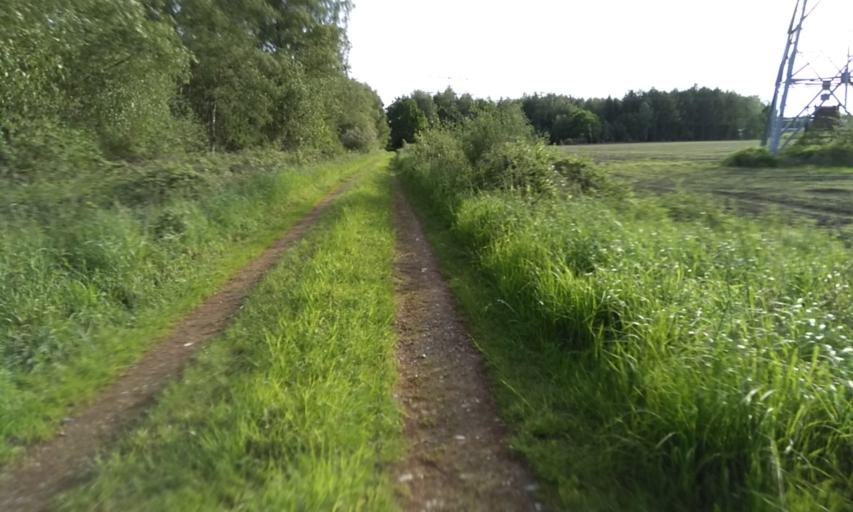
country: DE
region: Lower Saxony
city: Agathenburg
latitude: 53.5421
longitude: 9.5112
